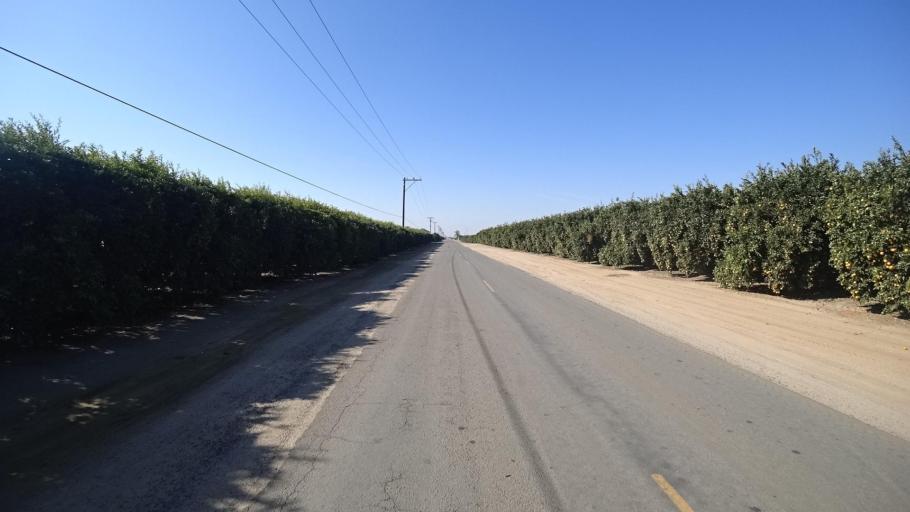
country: US
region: California
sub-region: Tulare County
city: Richgrove
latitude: 35.7185
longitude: -119.1368
